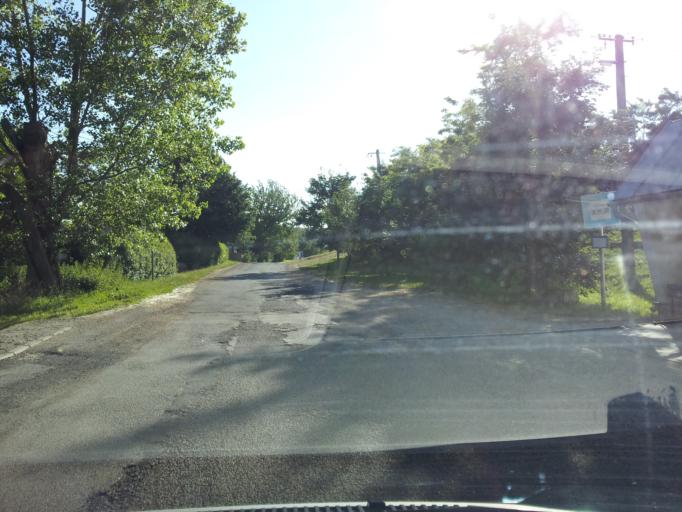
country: HU
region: Veszprem
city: Zirc
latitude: 47.2072
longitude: 17.8604
